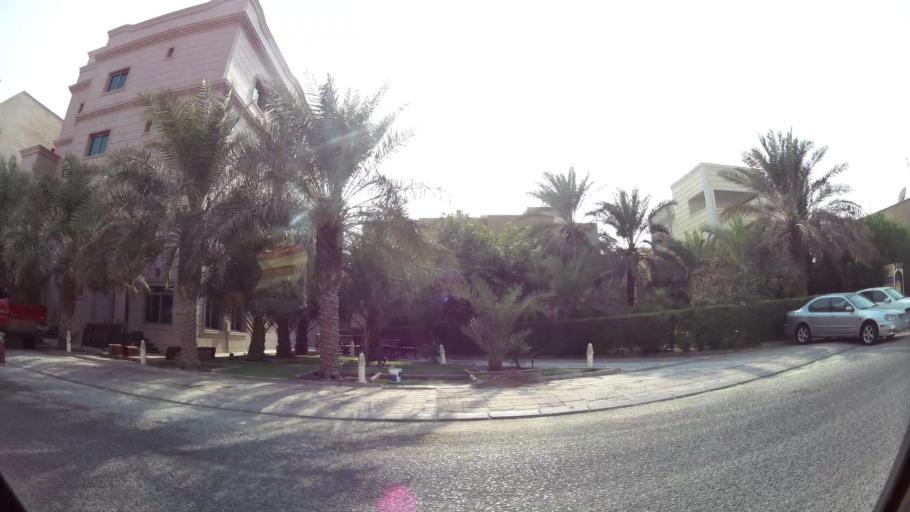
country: KW
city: Al Funaytis
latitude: 29.2208
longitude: 48.0807
